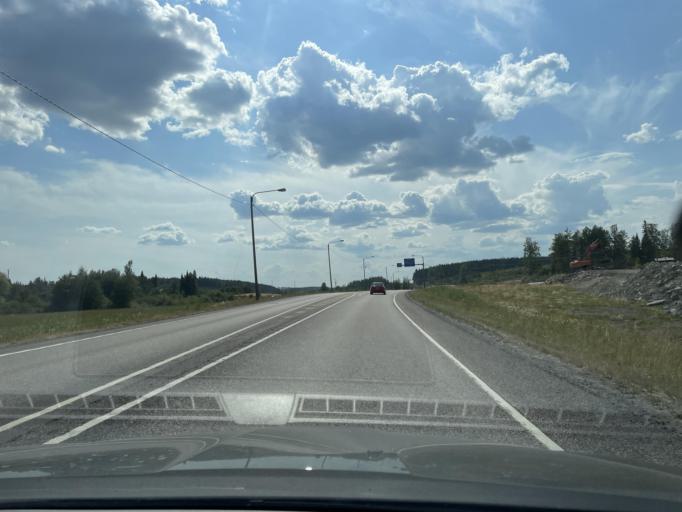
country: FI
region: Central Finland
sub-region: Jaemsae
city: Jaemsae
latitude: 61.8903
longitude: 25.2898
